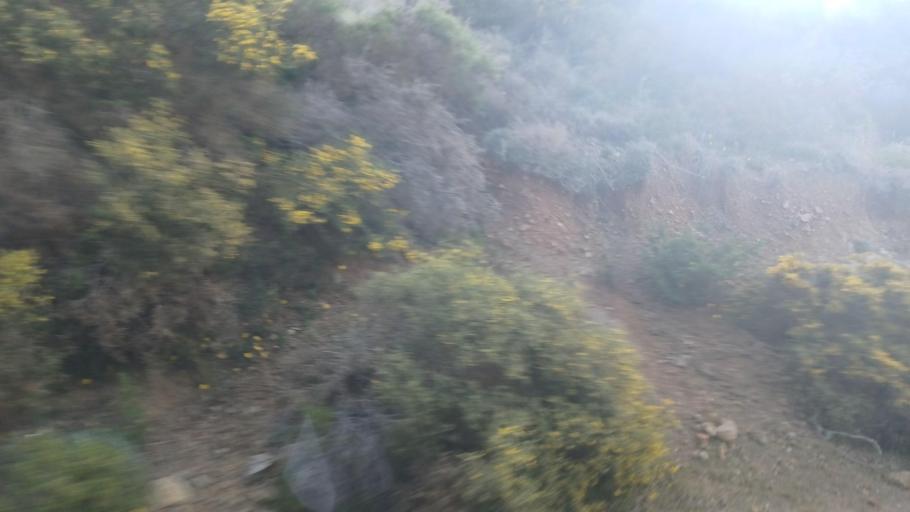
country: CY
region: Pafos
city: Polis
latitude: 35.0058
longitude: 32.3335
